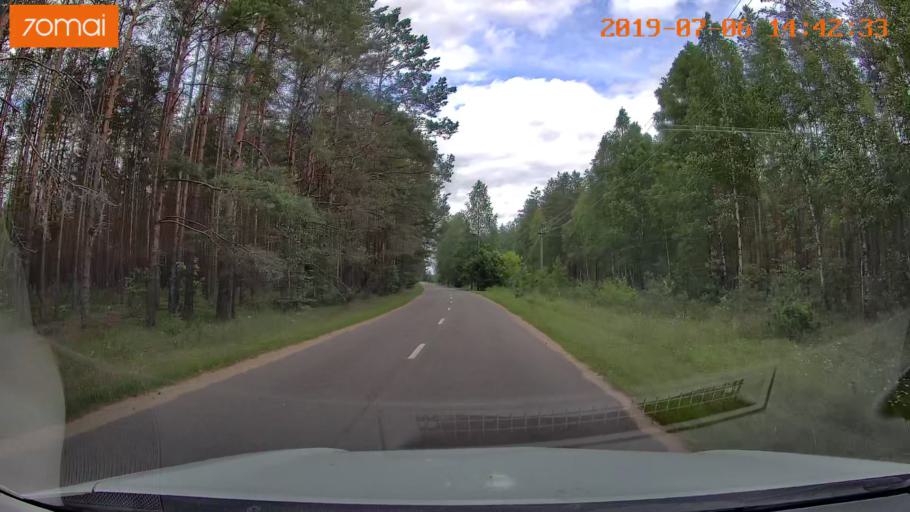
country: BY
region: Minsk
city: Ivyanyets
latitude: 53.9423
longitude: 26.6901
